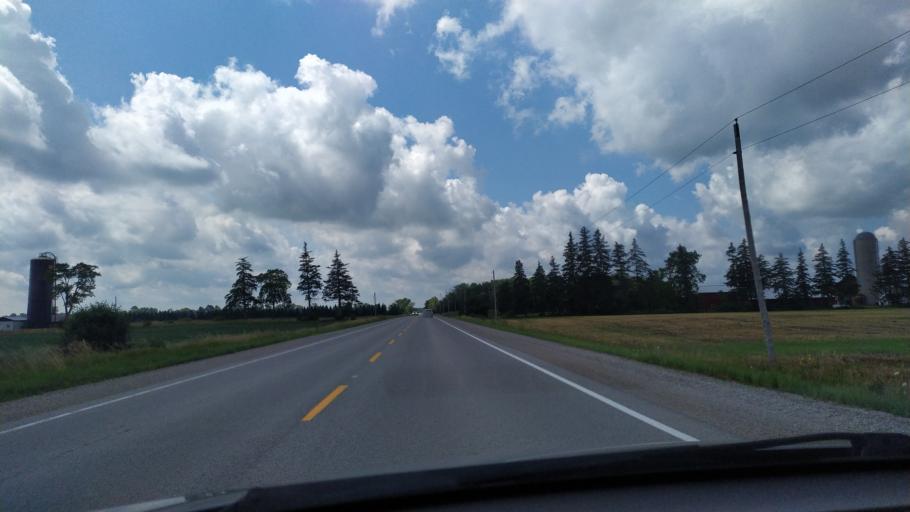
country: CA
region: Ontario
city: South Huron
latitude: 43.2841
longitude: -81.3468
